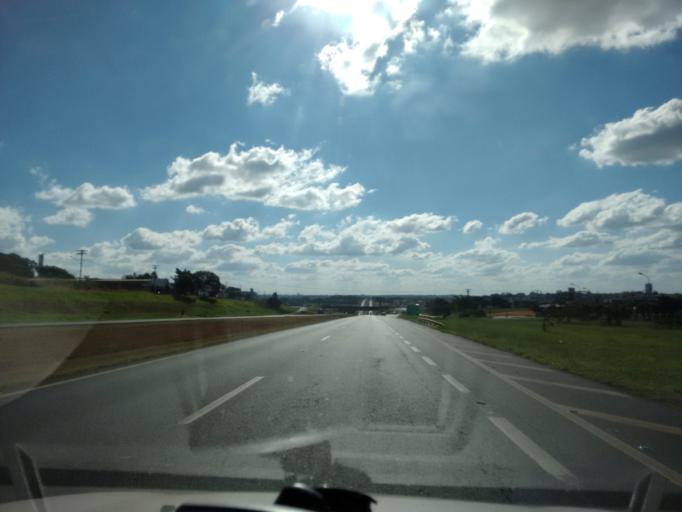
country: BR
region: Sao Paulo
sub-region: Araraquara
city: Araraquara
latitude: -21.8218
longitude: -48.1736
